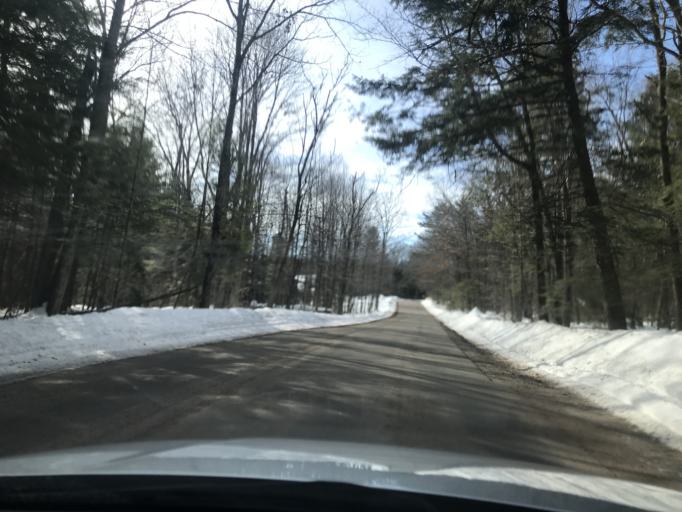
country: US
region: Wisconsin
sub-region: Menominee County
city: Legend Lake
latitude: 45.1215
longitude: -88.4273
